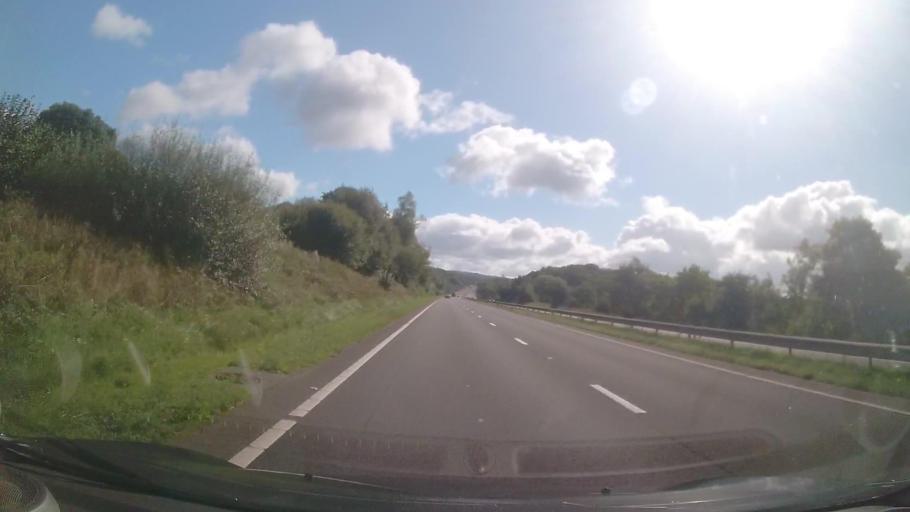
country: GB
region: Wales
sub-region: Carmarthenshire
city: Llanddarog
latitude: 51.8307
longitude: -4.1582
